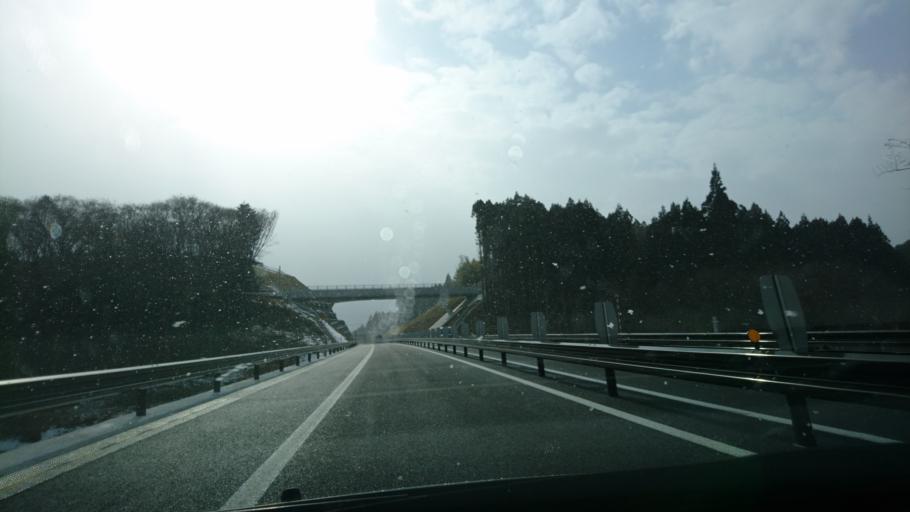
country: JP
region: Iwate
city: Ofunato
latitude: 38.8071
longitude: 141.5428
